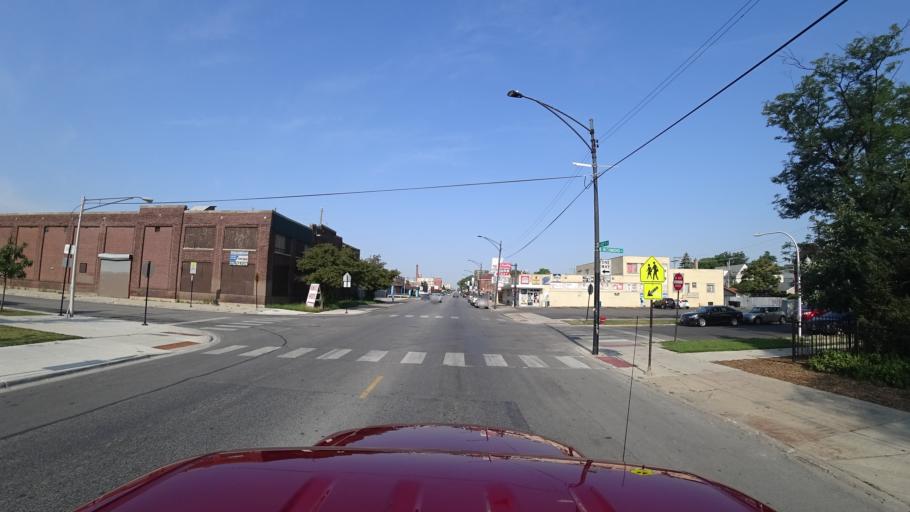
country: US
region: Illinois
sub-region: Cook County
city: Chicago
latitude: 41.8082
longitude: -87.6975
